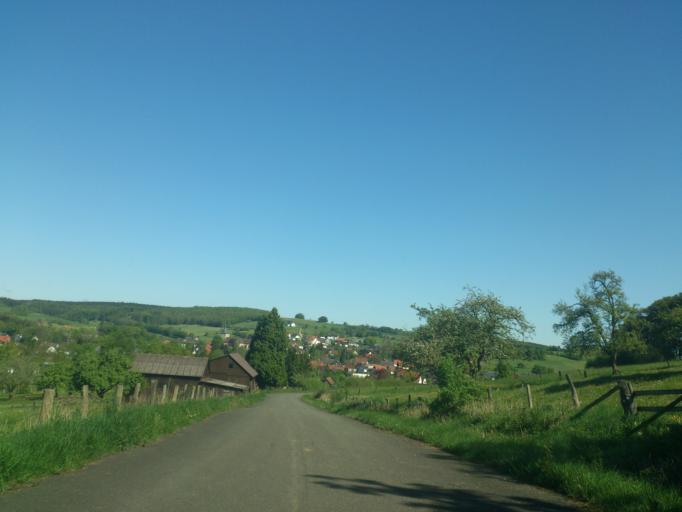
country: DE
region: North Rhine-Westphalia
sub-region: Regierungsbezirk Detmold
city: Willebadessen
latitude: 51.6678
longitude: 9.0052
